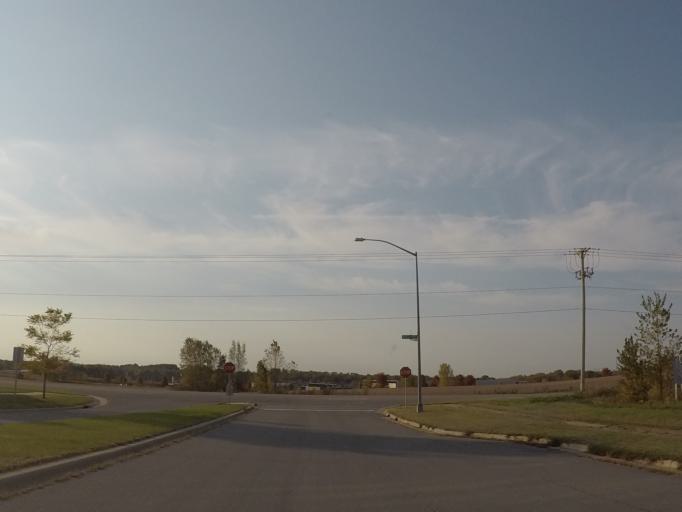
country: US
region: Wisconsin
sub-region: Dane County
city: Middleton
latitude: 43.0607
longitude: -89.5560
